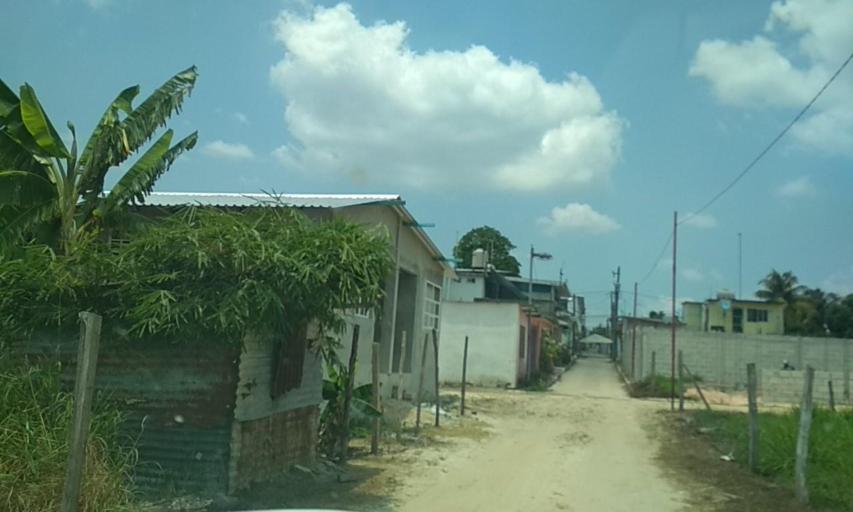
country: MX
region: Veracruz
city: Las Choapas
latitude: 17.9156
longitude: -94.0893
